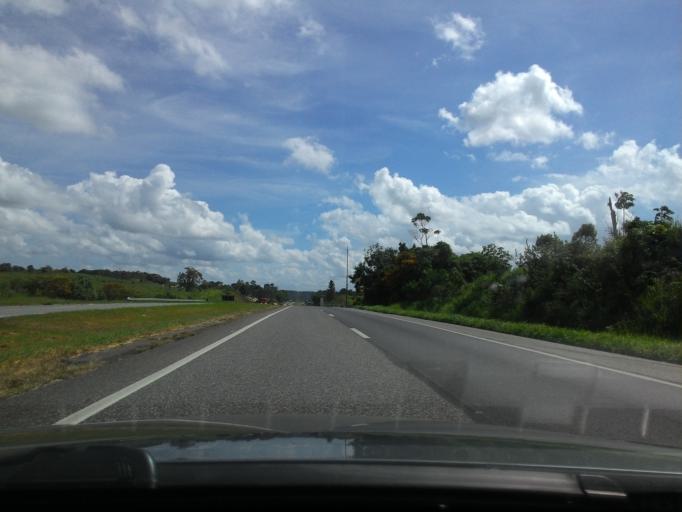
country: BR
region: Sao Paulo
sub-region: Pariquera-Acu
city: Pariquera Acu
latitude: -24.6338
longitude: -47.9076
